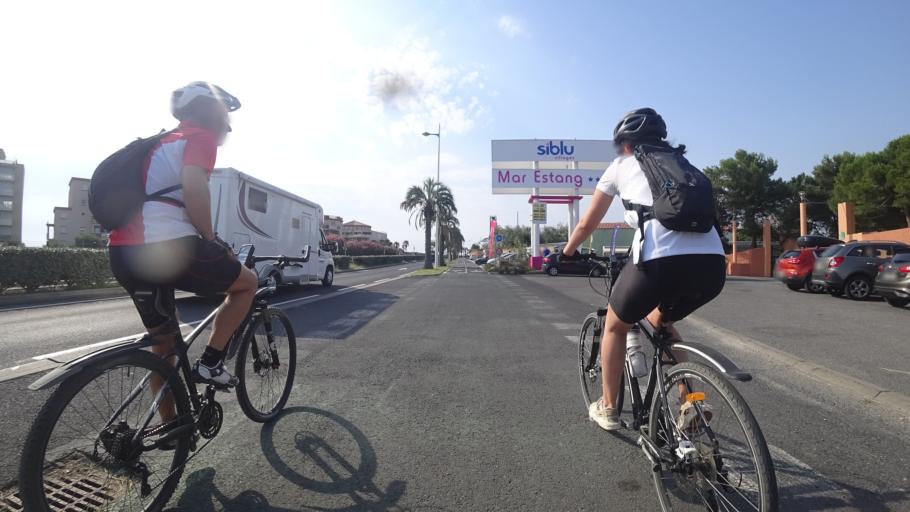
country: FR
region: Languedoc-Roussillon
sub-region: Departement des Pyrenees-Orientales
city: Canet-en-Roussillon
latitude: 42.6757
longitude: 3.0313
